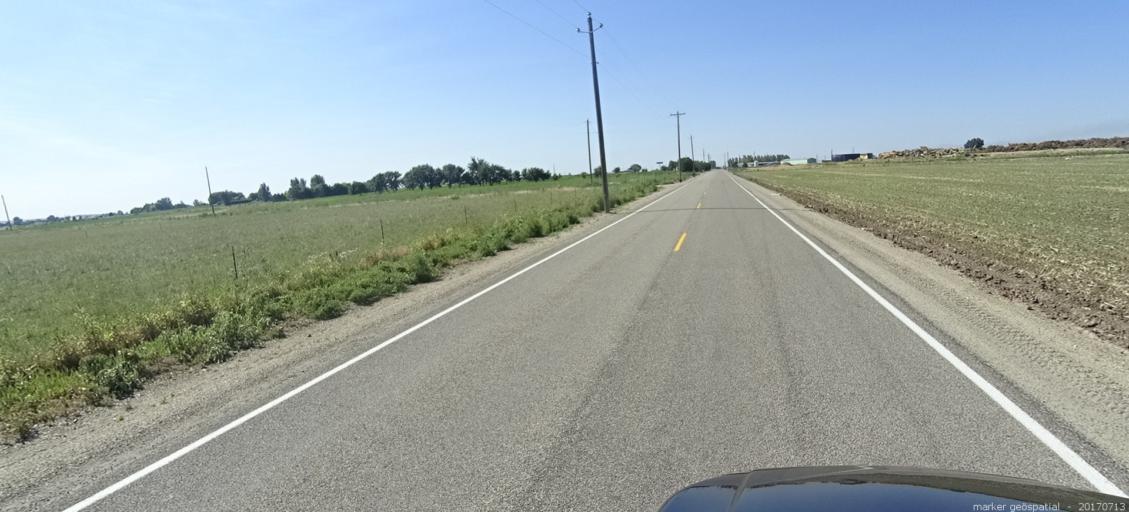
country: US
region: Idaho
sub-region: Ada County
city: Kuna
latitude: 43.5382
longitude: -116.3743
